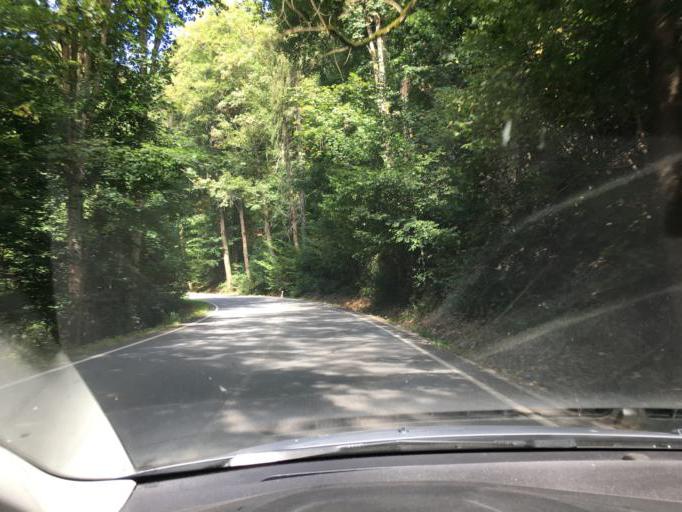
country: CZ
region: Liberecky
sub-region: Okres Semily
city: Ponikla
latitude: 50.6439
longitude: 15.4596
